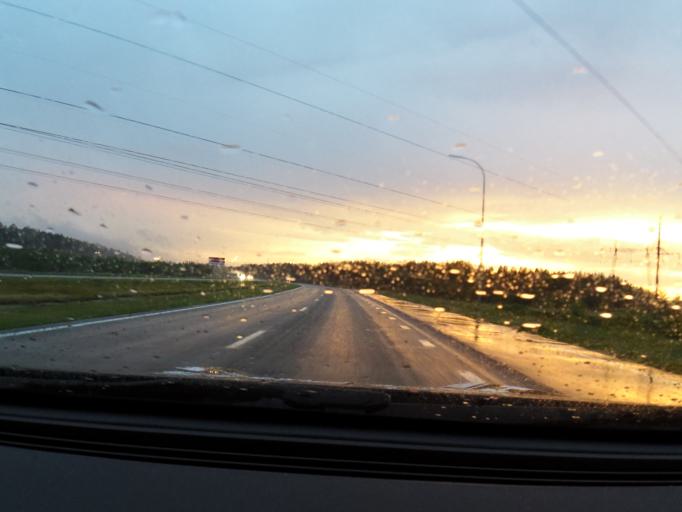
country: RU
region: Tatarstan
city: Yelabuga
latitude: 55.7801
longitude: 52.1970
